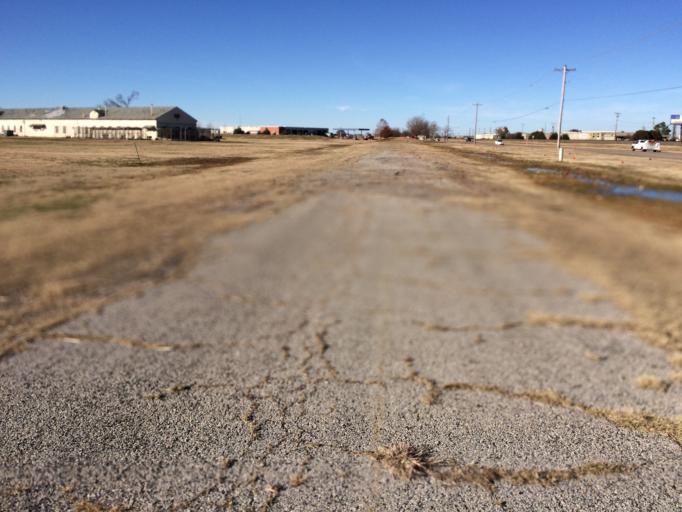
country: US
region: Oklahoma
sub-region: Cleveland County
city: Norman
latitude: 35.2416
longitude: -97.4576
